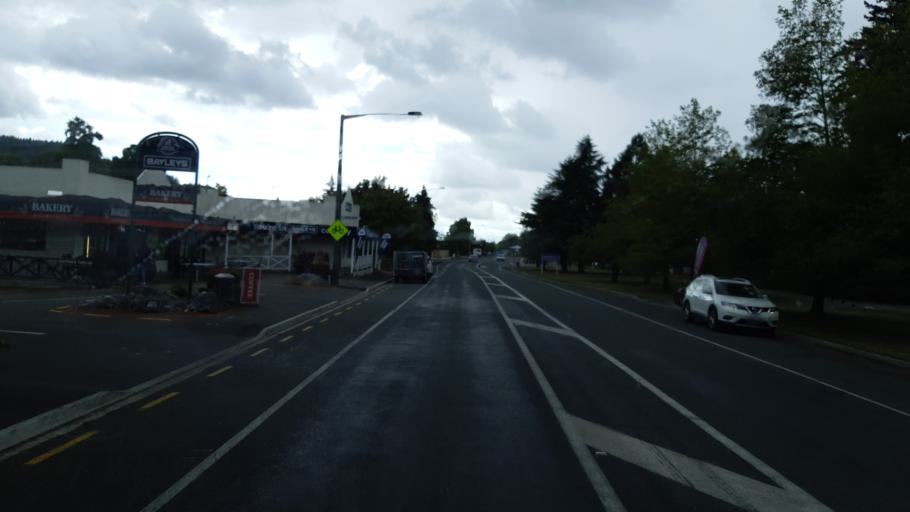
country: NZ
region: Tasman
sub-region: Tasman District
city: Wakefield
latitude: -41.4064
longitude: 173.0410
